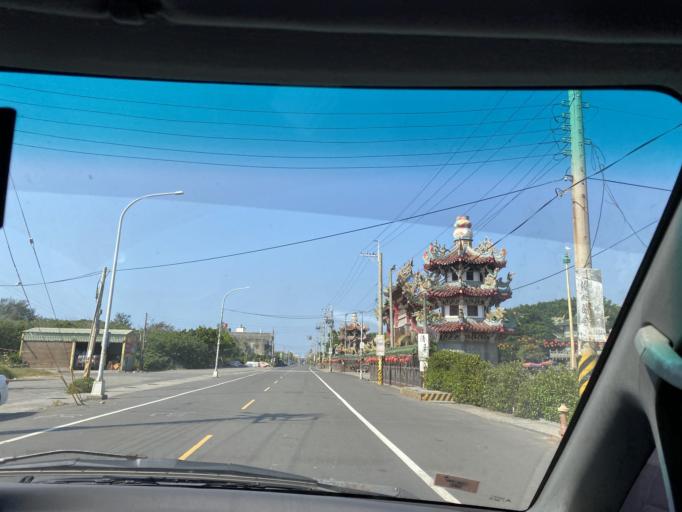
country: TW
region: Taiwan
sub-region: Changhua
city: Chang-hua
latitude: 23.9527
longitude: 120.3336
